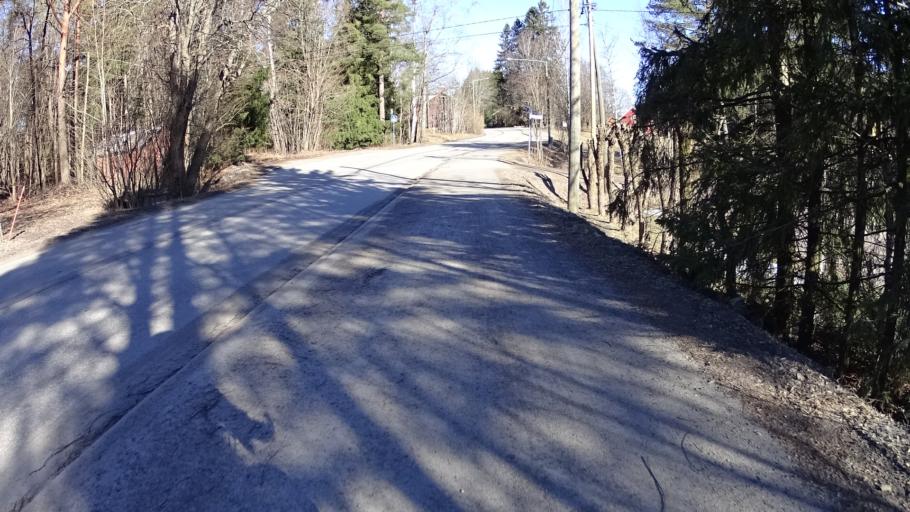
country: FI
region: Uusimaa
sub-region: Helsinki
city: Espoo
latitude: 60.2325
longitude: 24.6594
